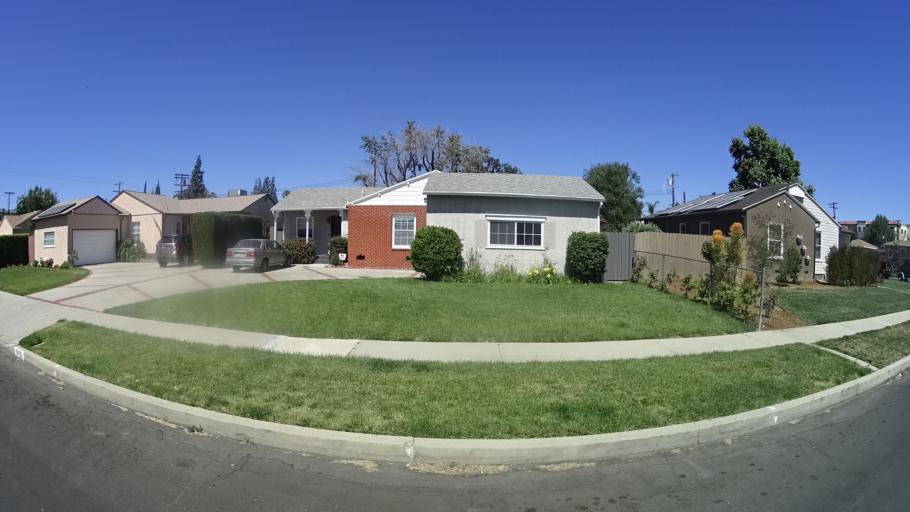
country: US
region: California
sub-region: Los Angeles County
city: San Fernando
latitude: 34.2543
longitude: -118.4658
